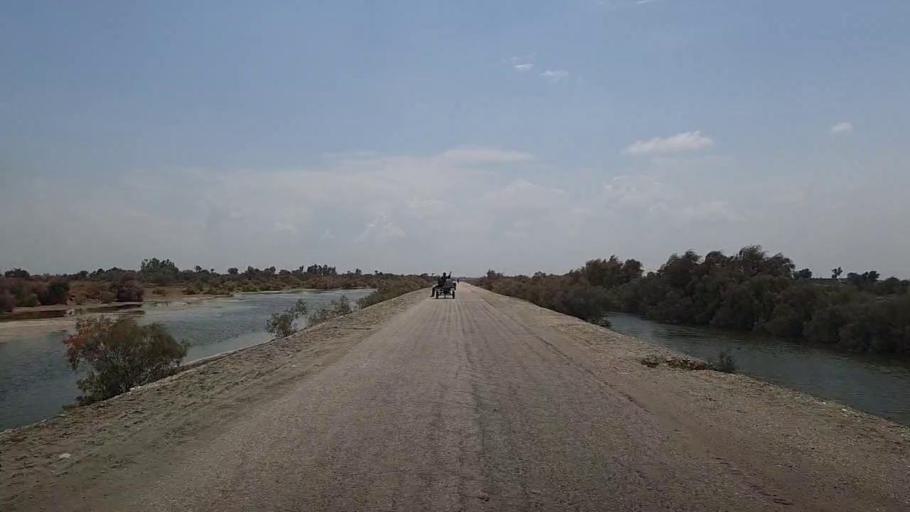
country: PK
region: Sindh
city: Kandhkot
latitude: 28.2846
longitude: 69.1673
